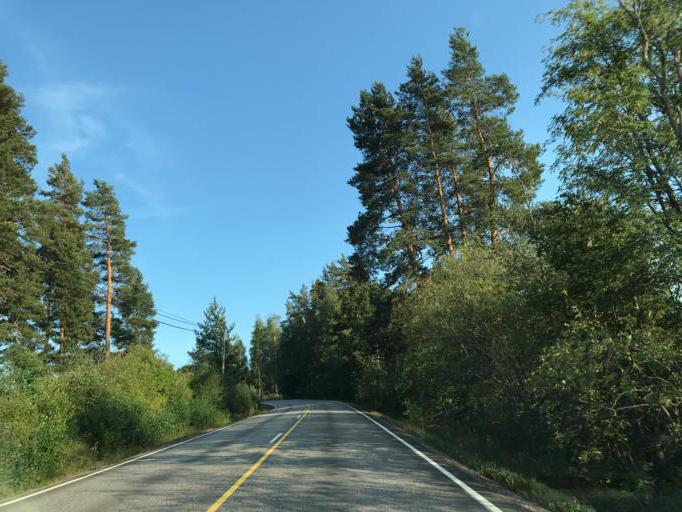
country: FI
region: Uusimaa
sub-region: Helsinki
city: Vihti
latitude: 60.4200
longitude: 24.3689
